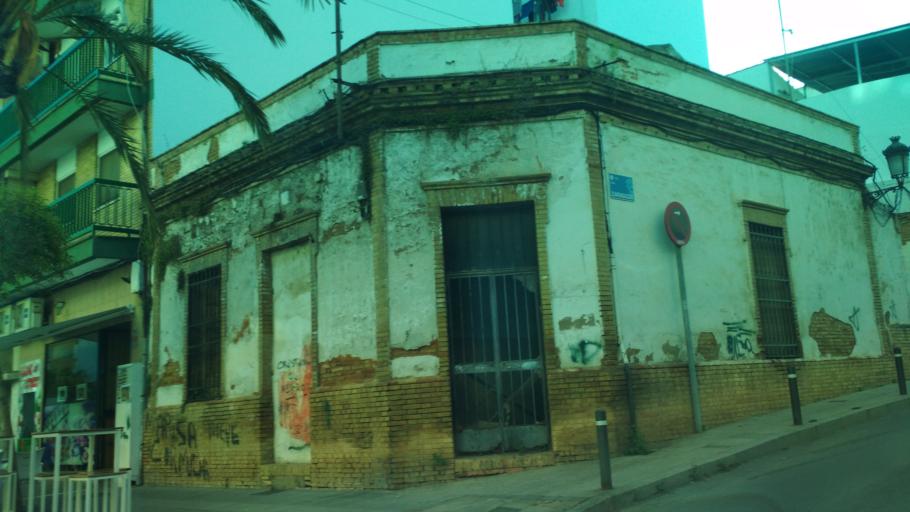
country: ES
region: Andalusia
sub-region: Provincia de Huelva
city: Huelva
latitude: 37.2712
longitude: -6.9504
